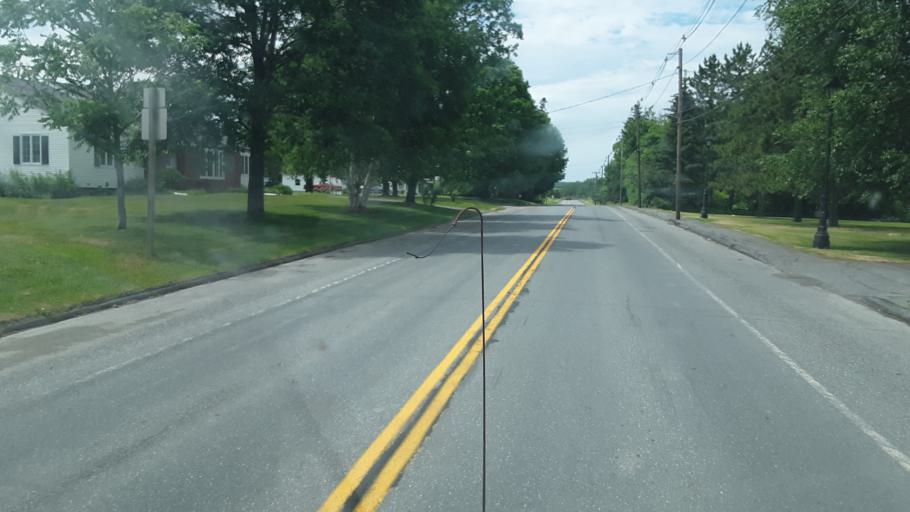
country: US
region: Maine
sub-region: Aroostook County
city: Fort Fairfield
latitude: 46.7741
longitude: -67.8382
